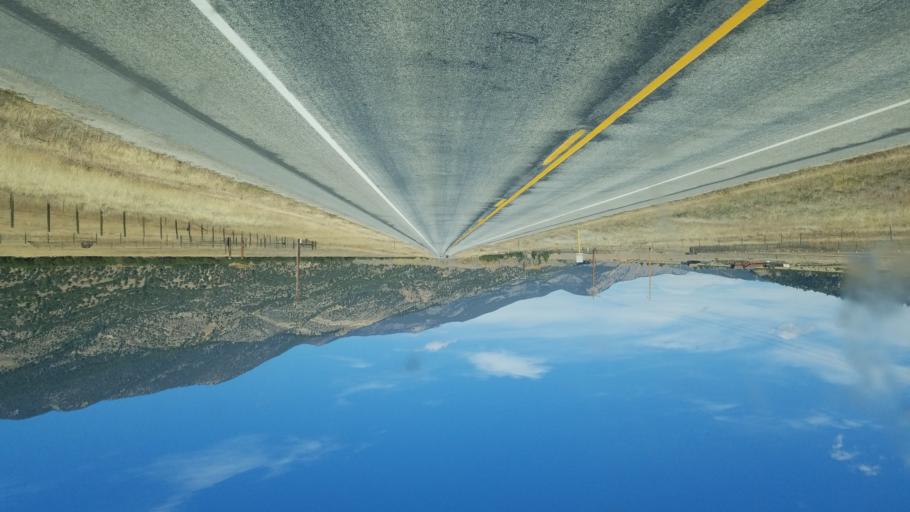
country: US
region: Colorado
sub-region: Chaffee County
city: Buena Vista
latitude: 38.9247
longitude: -106.1824
